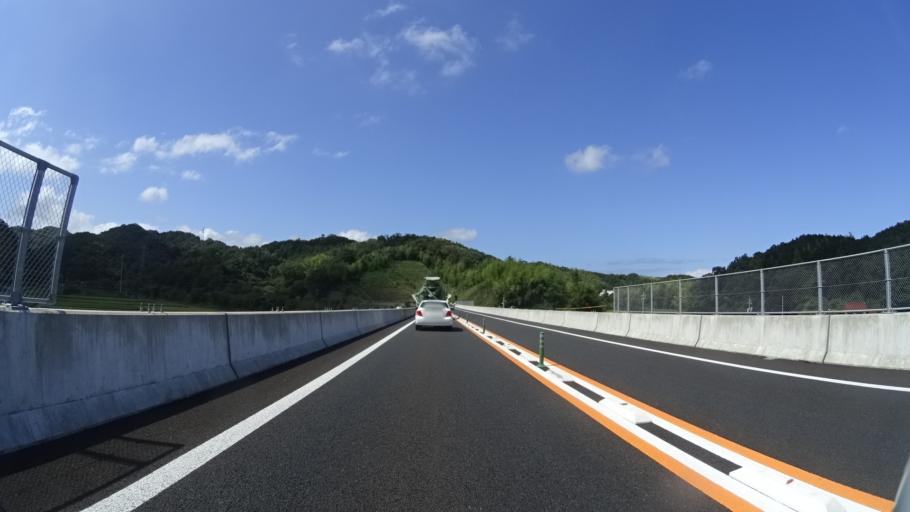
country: JP
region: Tottori
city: Tottori
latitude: 35.4957
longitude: 134.1750
